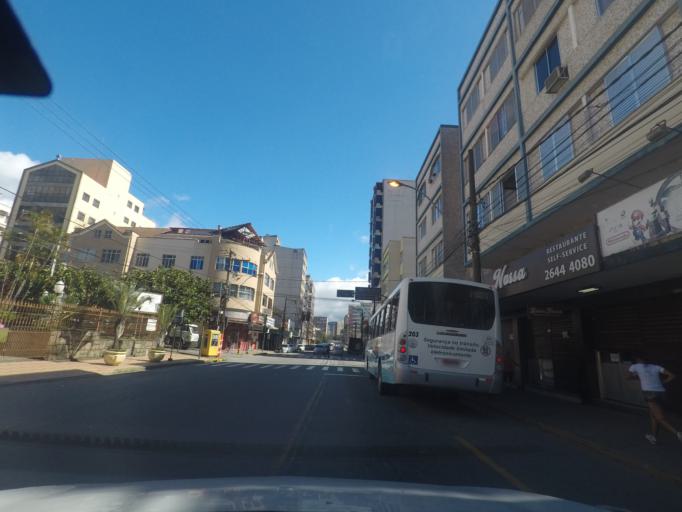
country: BR
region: Rio de Janeiro
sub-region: Teresopolis
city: Teresopolis
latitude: -22.4404
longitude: -42.9801
